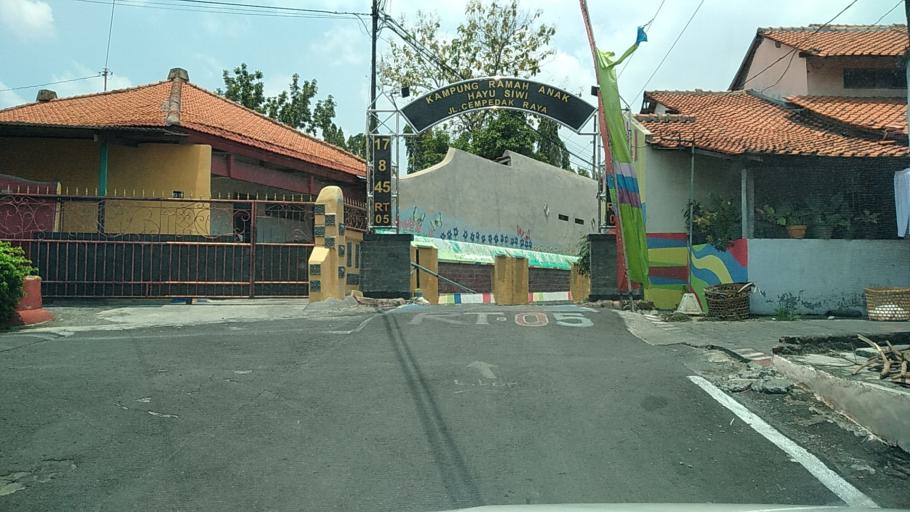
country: ID
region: Central Java
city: Semarang
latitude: -7.0015
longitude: 110.4394
